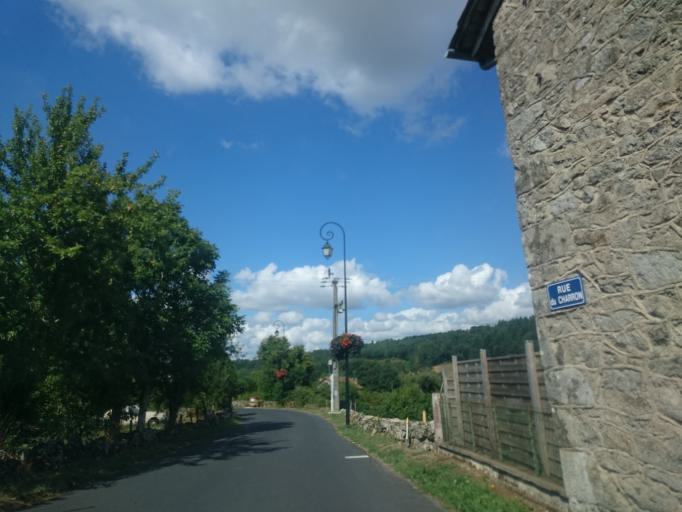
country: FR
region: Auvergne
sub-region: Departement du Cantal
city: Saint-Mamet-la-Salvetat
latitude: 44.8862
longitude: 2.2387
